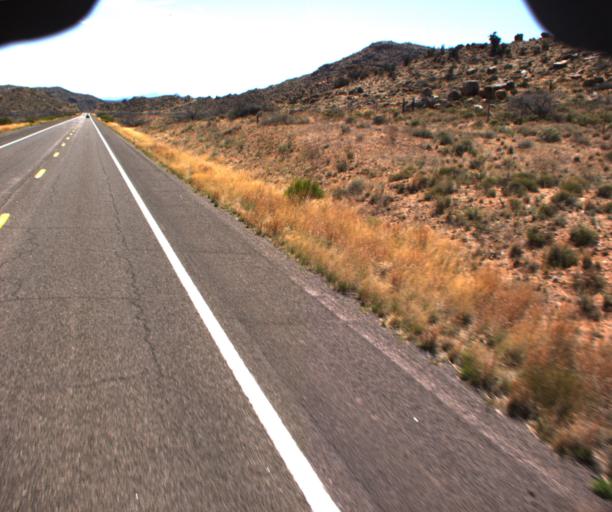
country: US
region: Arizona
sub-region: Mohave County
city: Peach Springs
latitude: 35.3795
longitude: -113.6648
